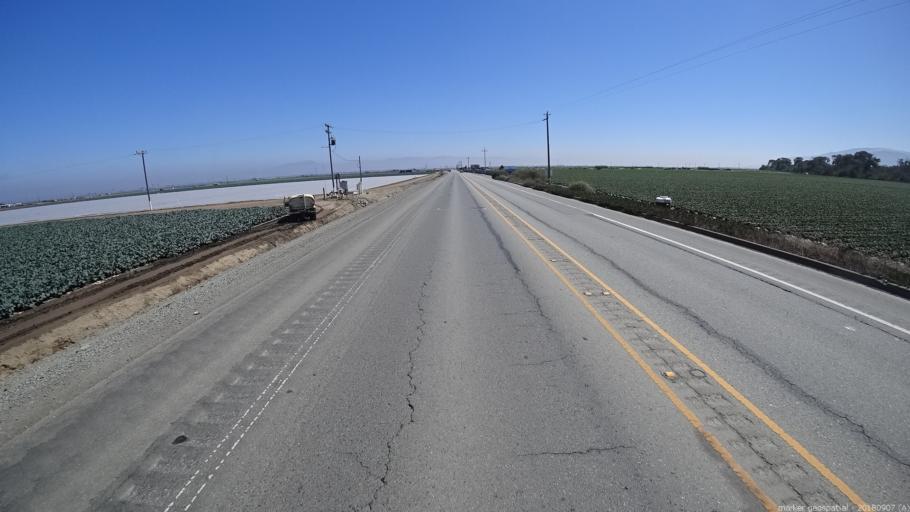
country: US
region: California
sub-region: Monterey County
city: Marina
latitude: 36.6785
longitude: -121.7402
